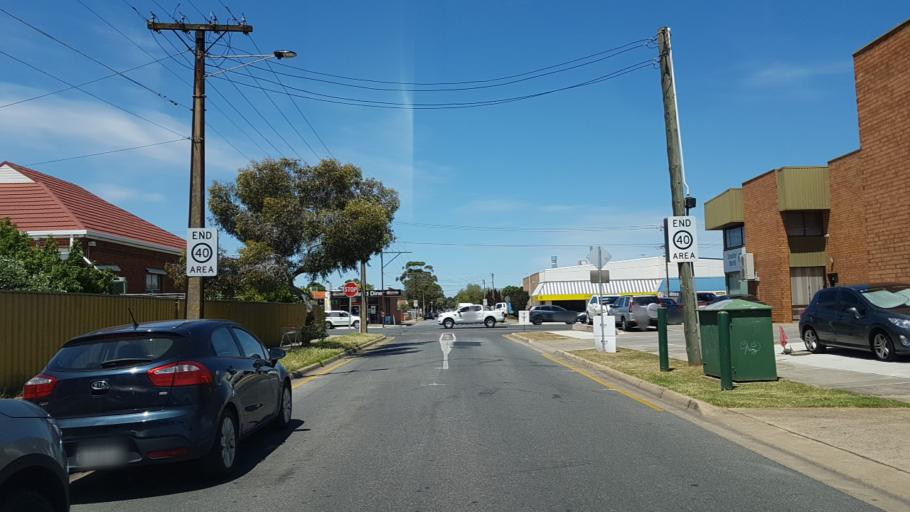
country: AU
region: South Australia
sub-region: Charles Sturt
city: Allenby Gardens
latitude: -34.9036
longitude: 138.5577
